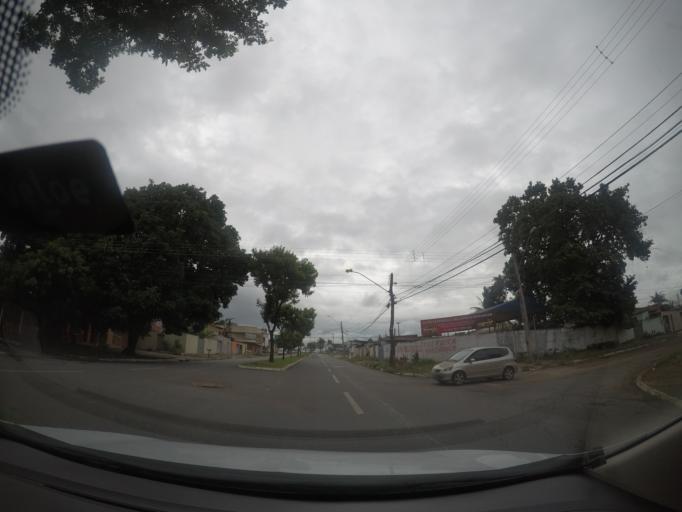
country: BR
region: Goias
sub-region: Goiania
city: Goiania
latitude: -16.7361
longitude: -49.2744
